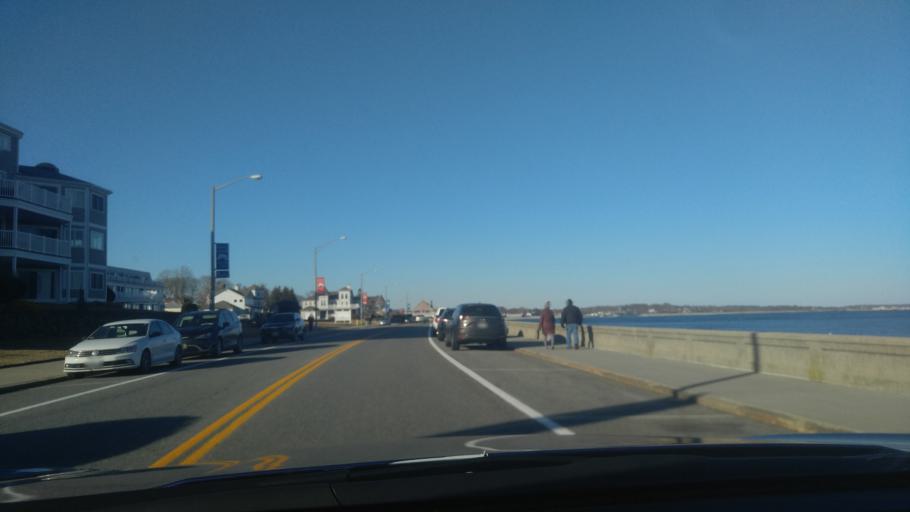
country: US
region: Rhode Island
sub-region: Washington County
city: Narragansett Pier
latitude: 41.4268
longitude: -71.4560
